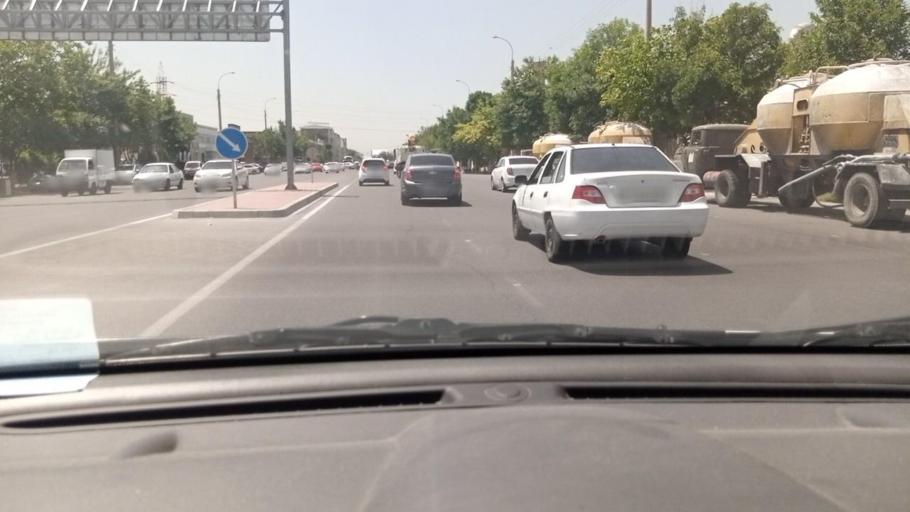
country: UZ
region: Toshkent Shahri
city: Tashkent
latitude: 41.2646
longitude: 69.2364
